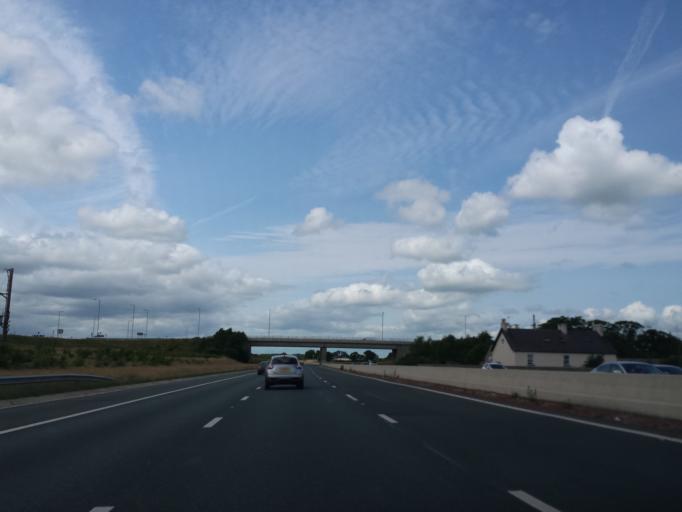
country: GB
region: England
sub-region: North Yorkshire
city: Bedale
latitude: 54.2712
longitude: -1.5256
